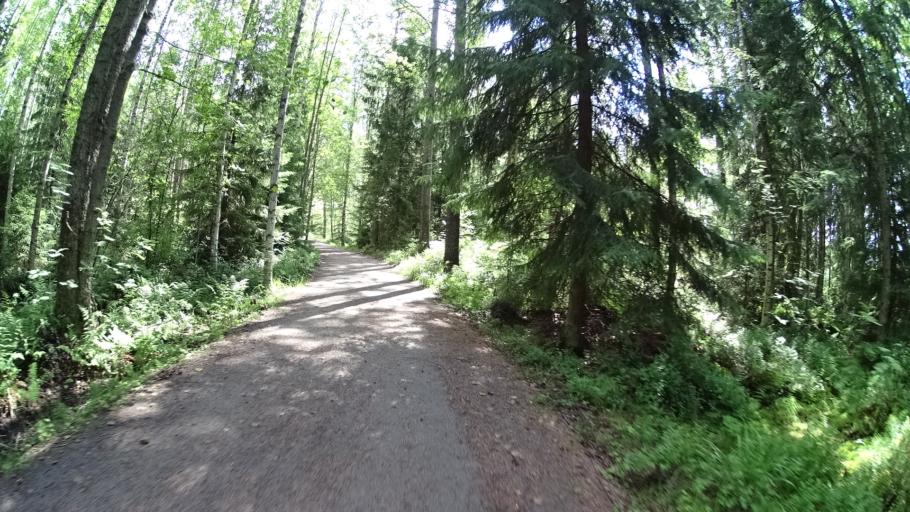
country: FI
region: Uusimaa
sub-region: Helsinki
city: Espoo
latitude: 60.3204
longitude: 24.6767
